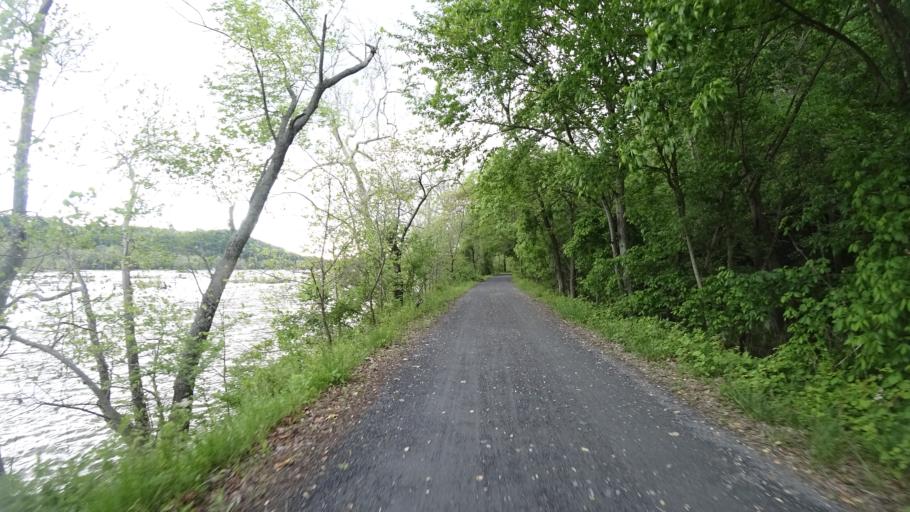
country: US
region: West Virginia
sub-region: Jefferson County
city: Bolivar
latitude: 39.3337
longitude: -77.7409
